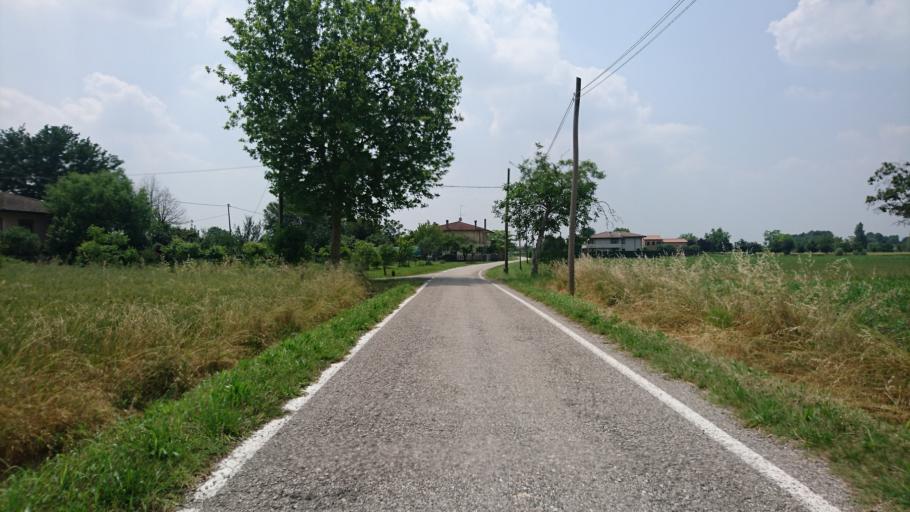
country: IT
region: Veneto
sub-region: Provincia di Padova
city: Cartura
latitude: 45.2683
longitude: 11.8826
